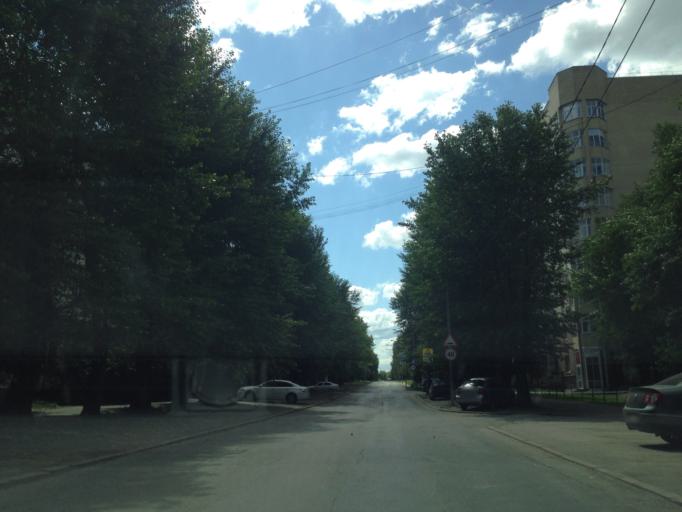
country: RU
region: Sverdlovsk
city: Yekaterinburg
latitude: 56.8466
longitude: 60.6545
